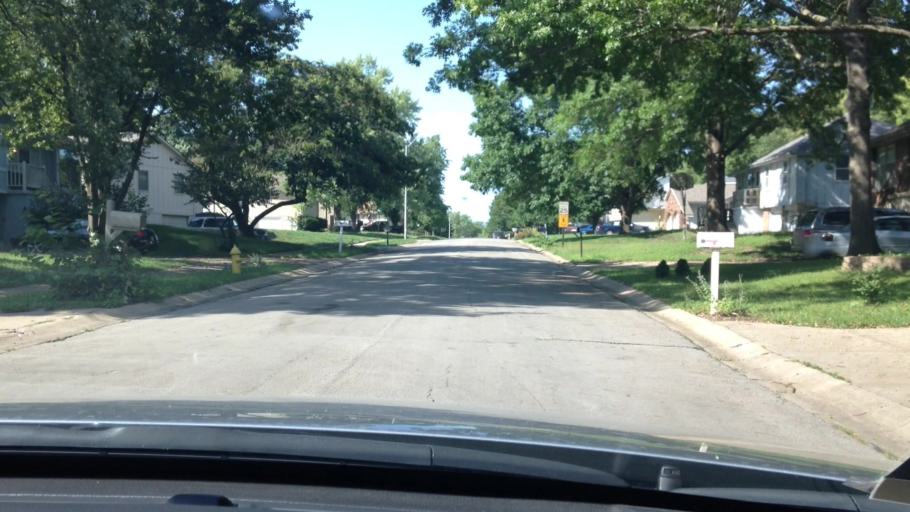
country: US
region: Missouri
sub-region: Jackson County
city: Grandview
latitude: 38.8794
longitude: -94.5041
